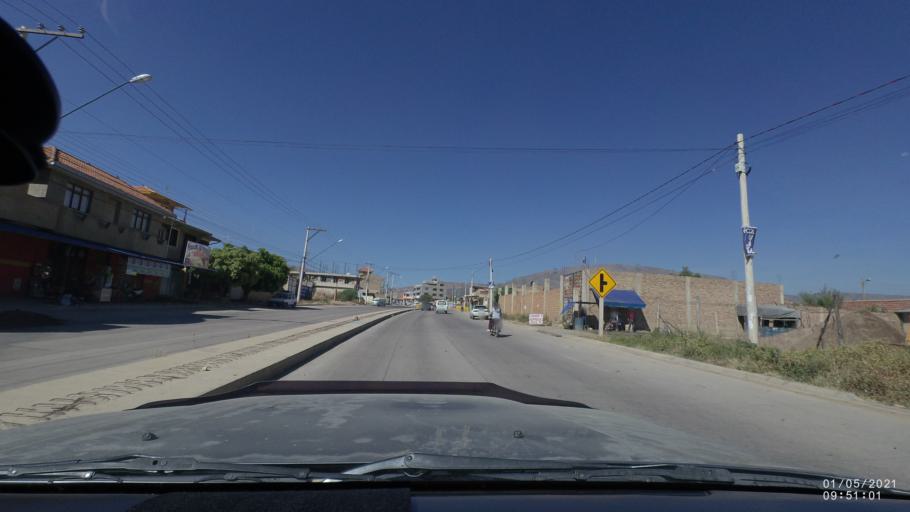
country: BO
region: Cochabamba
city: Cochabamba
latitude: -17.4690
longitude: -66.1706
